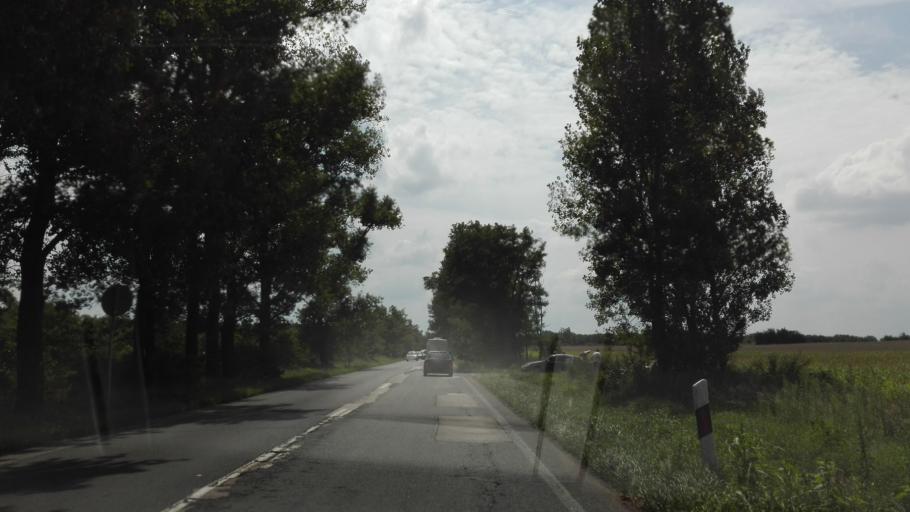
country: HU
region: Fejer
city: Alap
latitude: 46.7808
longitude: 18.6720
